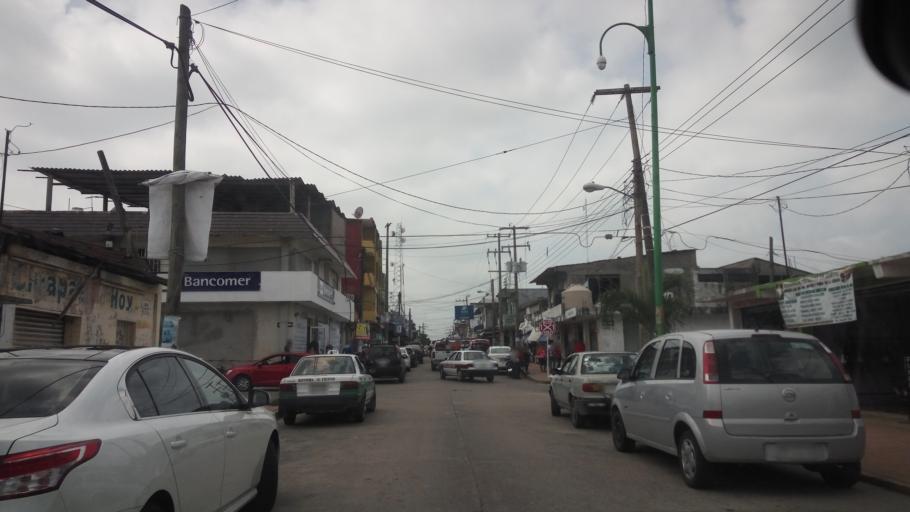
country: MX
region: Chiapas
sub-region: Reforma
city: El Carmen (El Limon)
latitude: 17.8679
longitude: -93.1484
